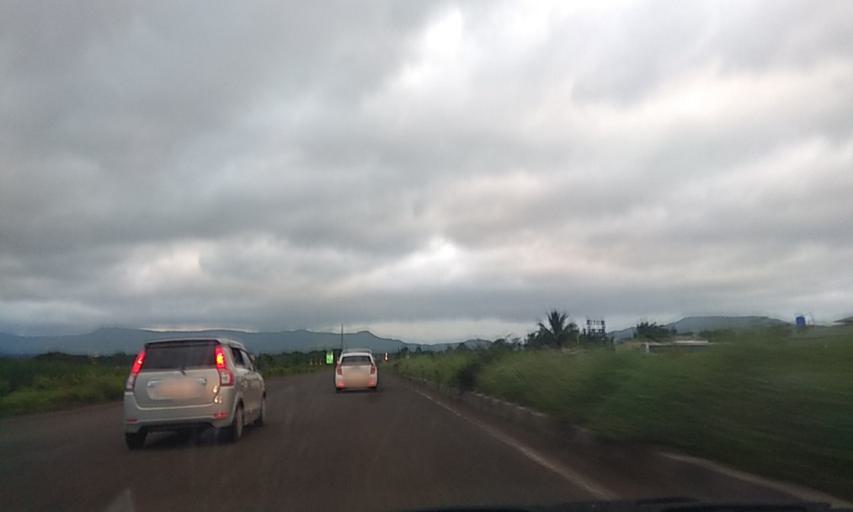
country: IN
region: Maharashtra
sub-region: Satara Division
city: Wai
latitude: 17.9383
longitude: 73.9771
